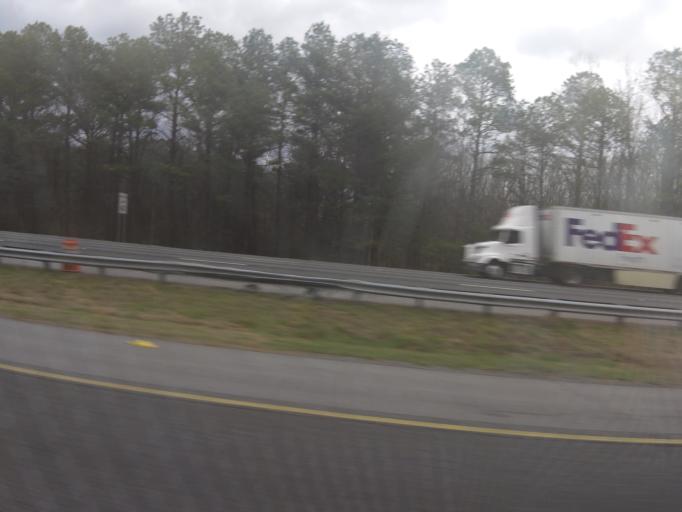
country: US
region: Georgia
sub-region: Whitfield County
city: Dalton
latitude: 34.6396
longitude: -84.9785
